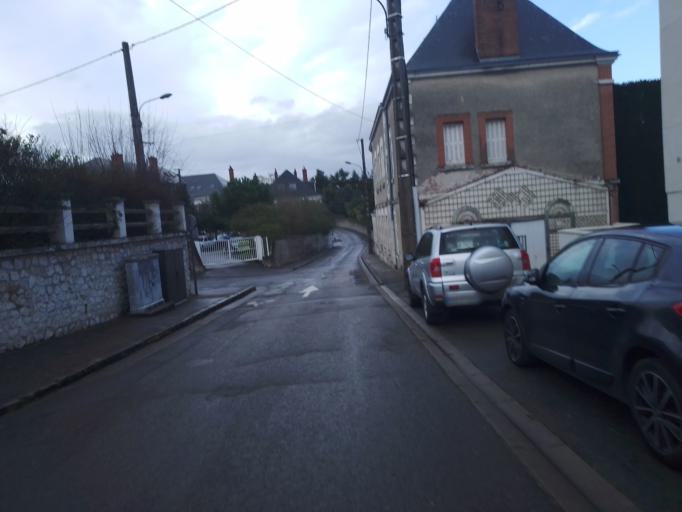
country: FR
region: Centre
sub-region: Departement du Loir-et-Cher
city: Blois
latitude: 47.5951
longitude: 1.3455
